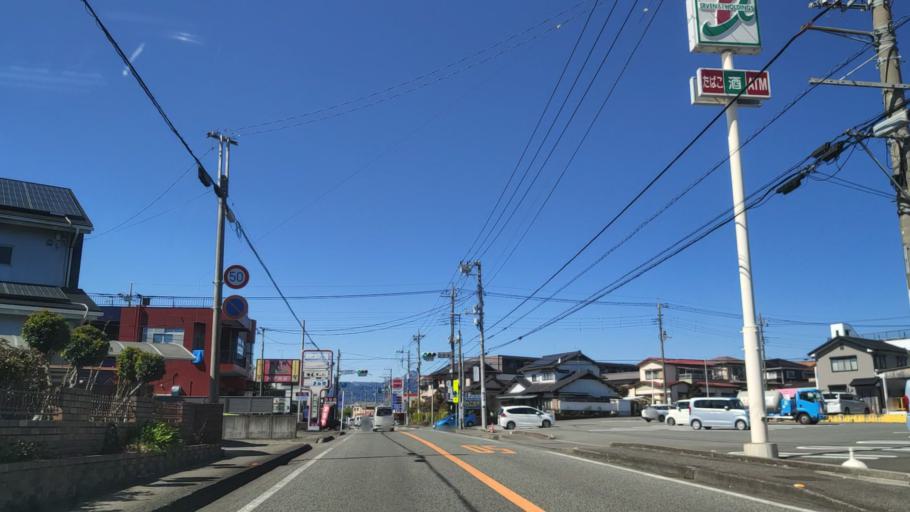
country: JP
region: Shizuoka
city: Fujinomiya
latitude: 35.2093
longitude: 138.6376
